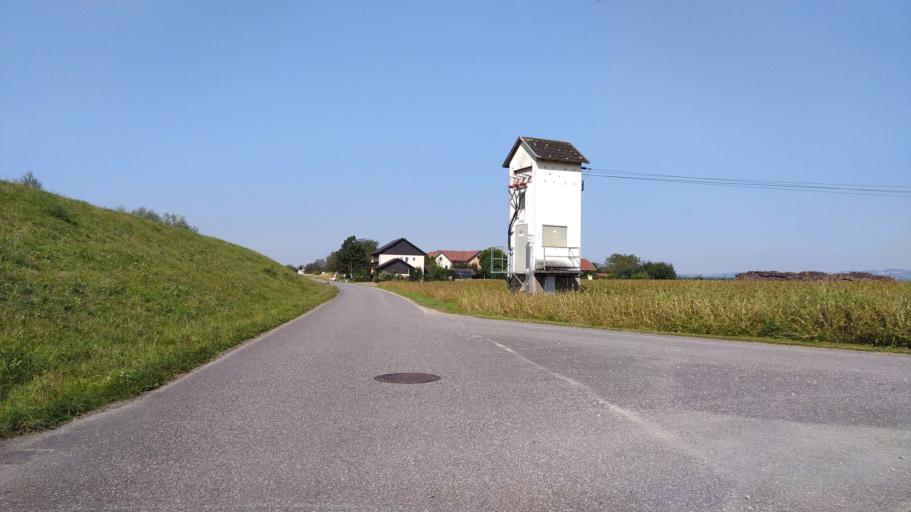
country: AT
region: Lower Austria
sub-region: Politischer Bezirk Amstetten
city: Strengberg
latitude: 48.1903
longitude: 14.7160
